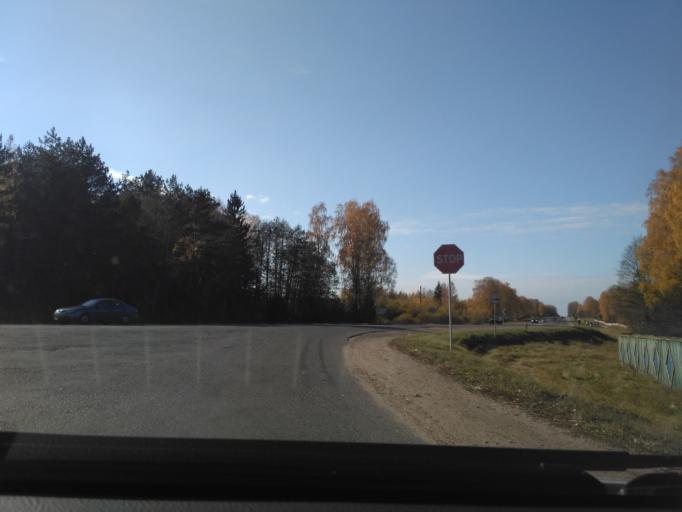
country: BY
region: Minsk
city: Horad Barysaw
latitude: 54.2558
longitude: 28.5726
